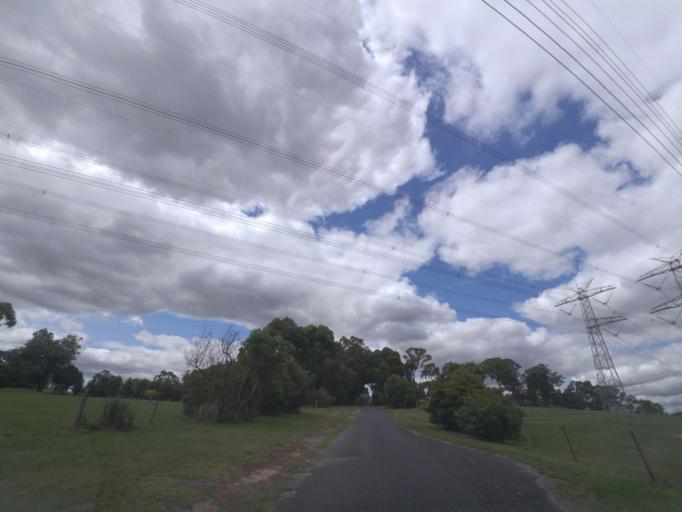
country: AU
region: Victoria
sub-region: Manningham
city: Park Orchards
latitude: -37.7839
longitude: 145.1997
